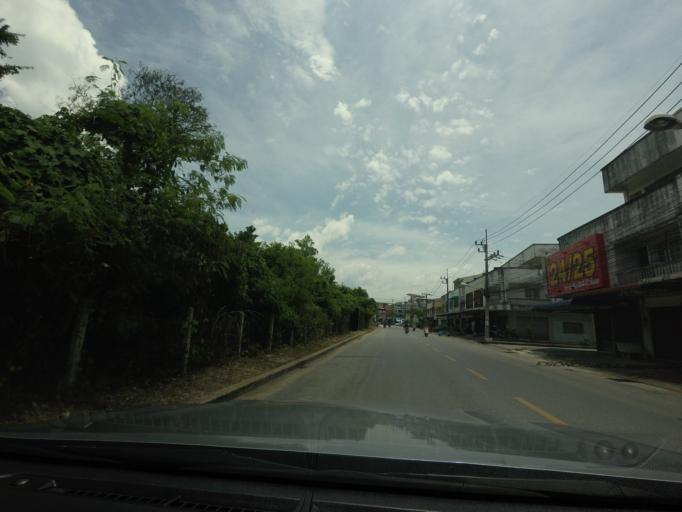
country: TH
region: Yala
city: Yala
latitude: 6.5469
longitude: 101.2939
